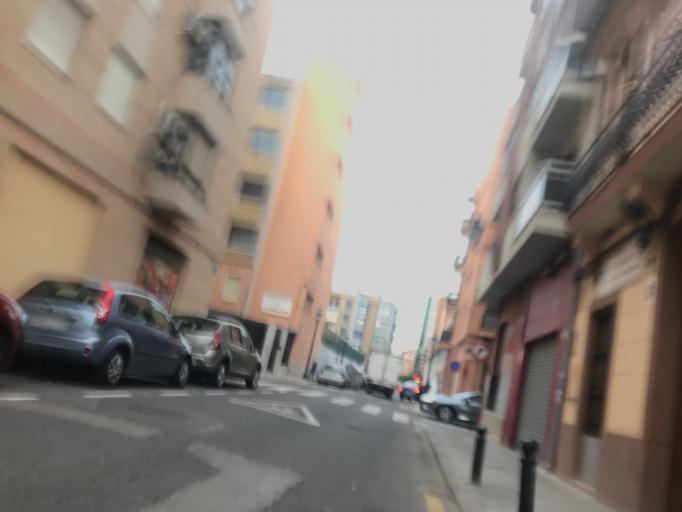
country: ES
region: Valencia
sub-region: Provincia de Valencia
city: Valencia
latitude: 39.4649
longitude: -0.3447
